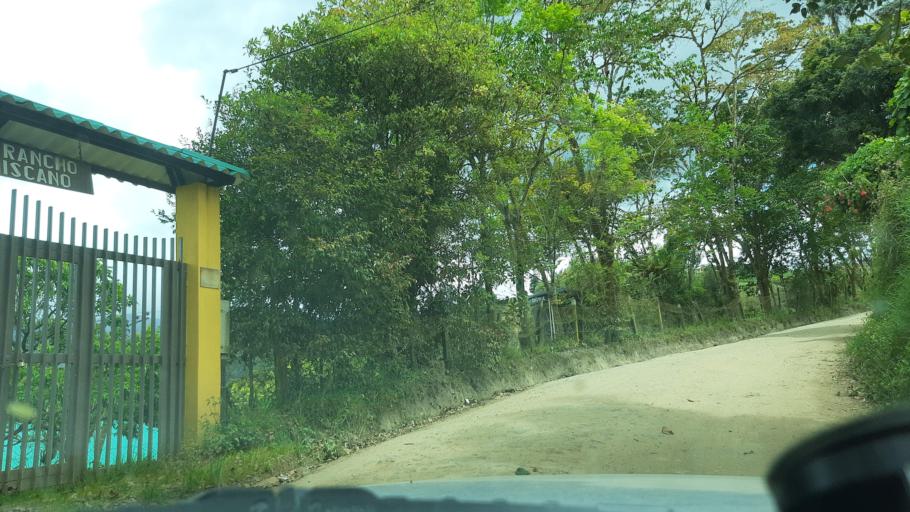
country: CO
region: Cundinamarca
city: Umbita
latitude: 5.2219
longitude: -73.4511
